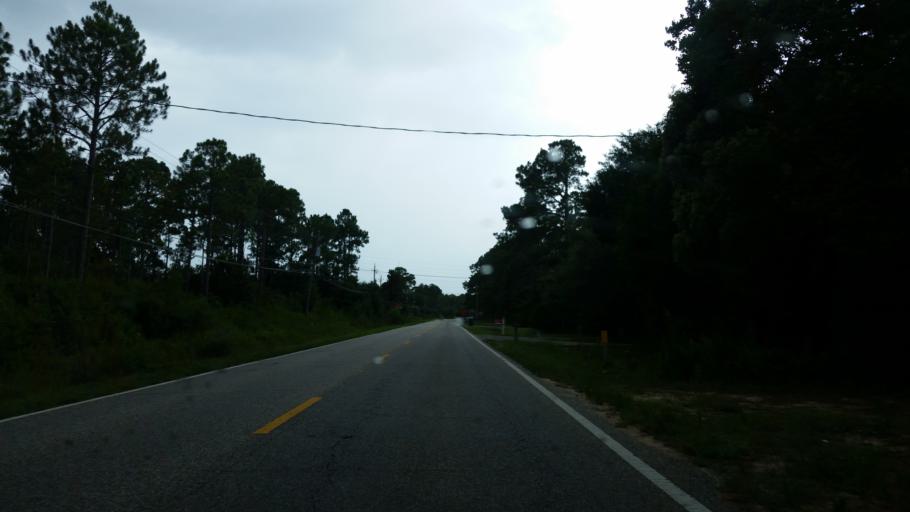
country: US
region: Florida
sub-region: Santa Rosa County
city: Woodlawn Beach
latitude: 30.4230
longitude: -86.9730
